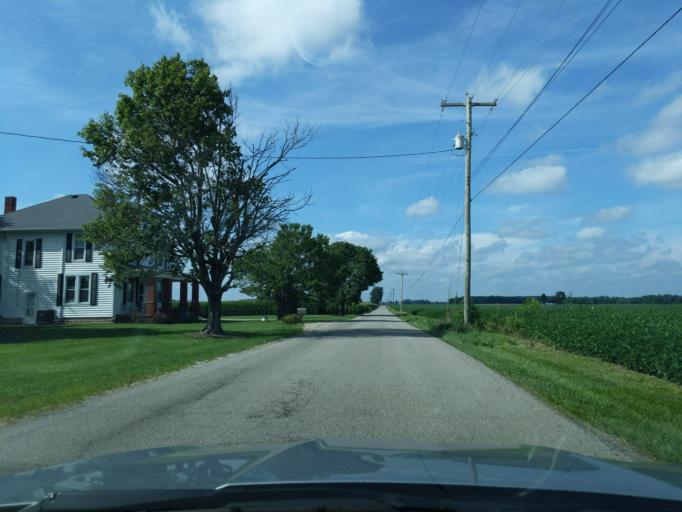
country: US
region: Indiana
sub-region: Ripley County
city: Batesville
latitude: 39.2798
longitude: -85.3476
